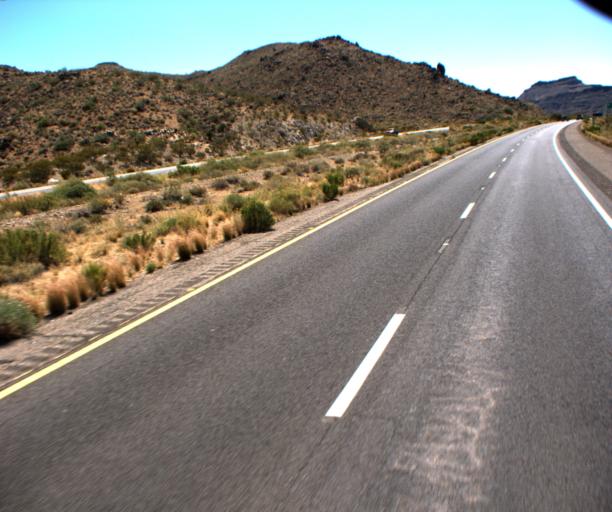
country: US
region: Arizona
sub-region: Mohave County
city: Golden Valley
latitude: 35.2336
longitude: -114.1385
